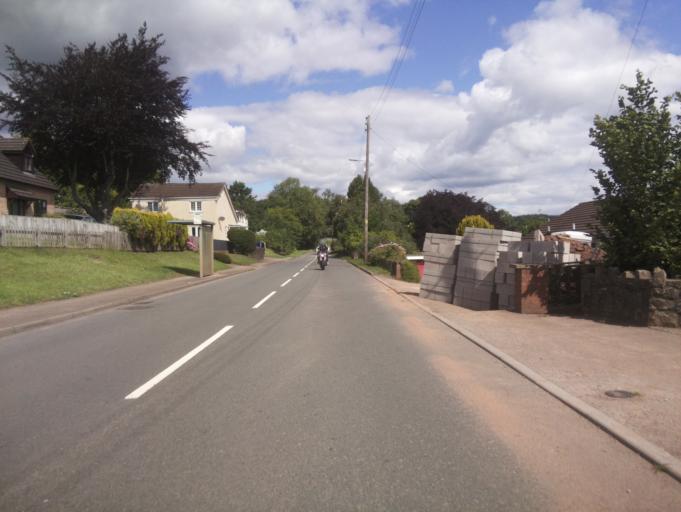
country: GB
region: England
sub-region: Gloucestershire
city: Lydney
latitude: 51.7290
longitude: -2.5384
